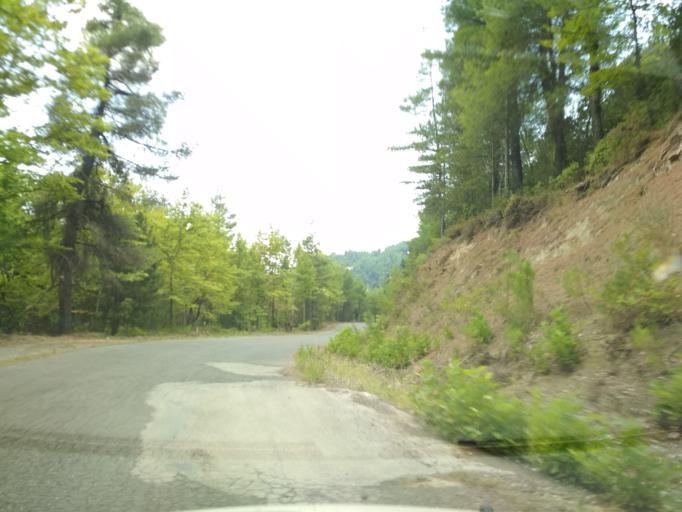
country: GR
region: Central Greece
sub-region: Nomos Evvoias
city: Roviai
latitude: 38.8534
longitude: 23.2831
